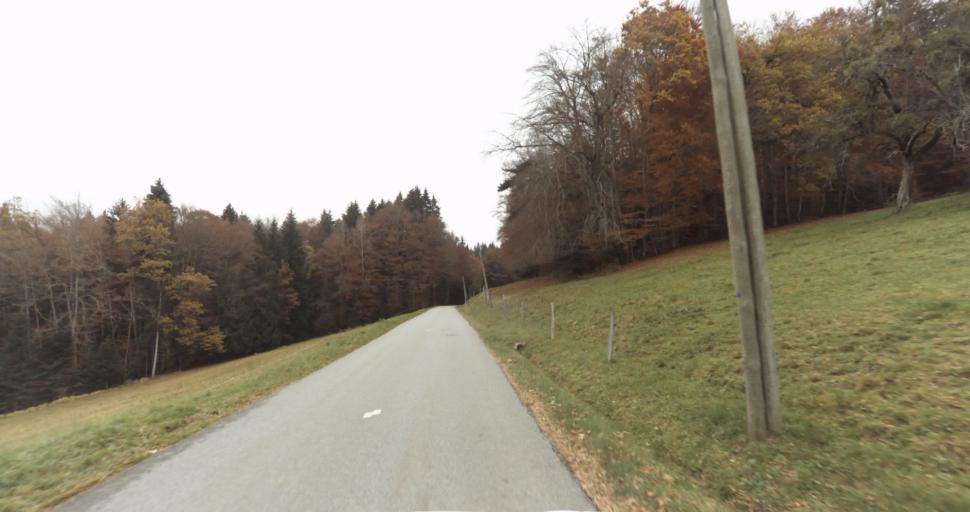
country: FR
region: Rhone-Alpes
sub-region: Departement de la Haute-Savoie
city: Gruffy
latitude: 45.7555
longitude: 6.1273
